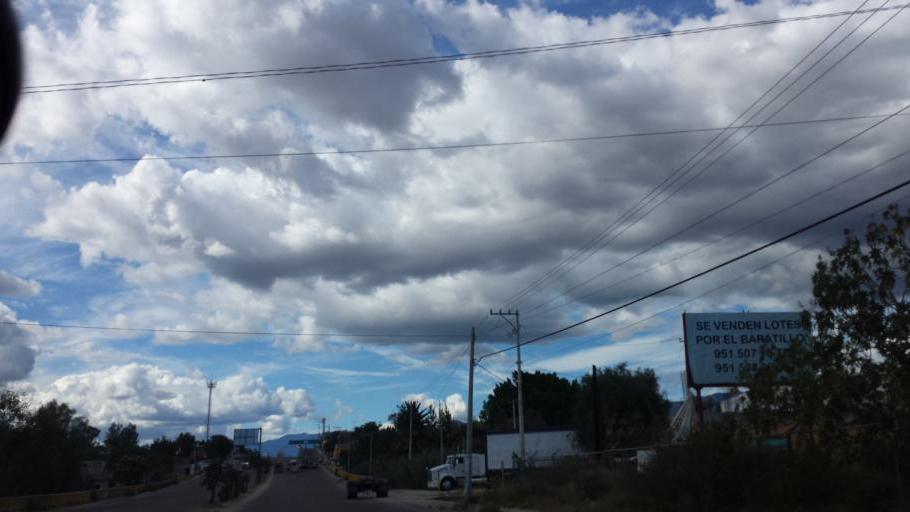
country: MX
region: Oaxaca
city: Tlacolula de Matamoros
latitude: 16.9555
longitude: -96.4711
